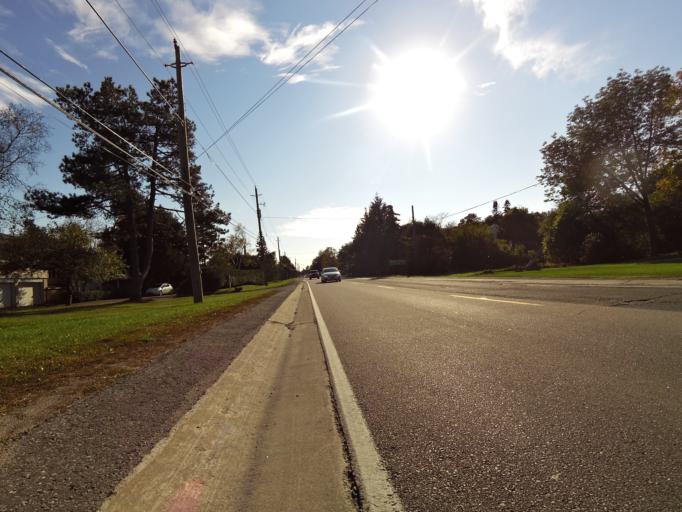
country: CA
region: Ontario
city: Kingston
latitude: 44.2290
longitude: -76.6268
